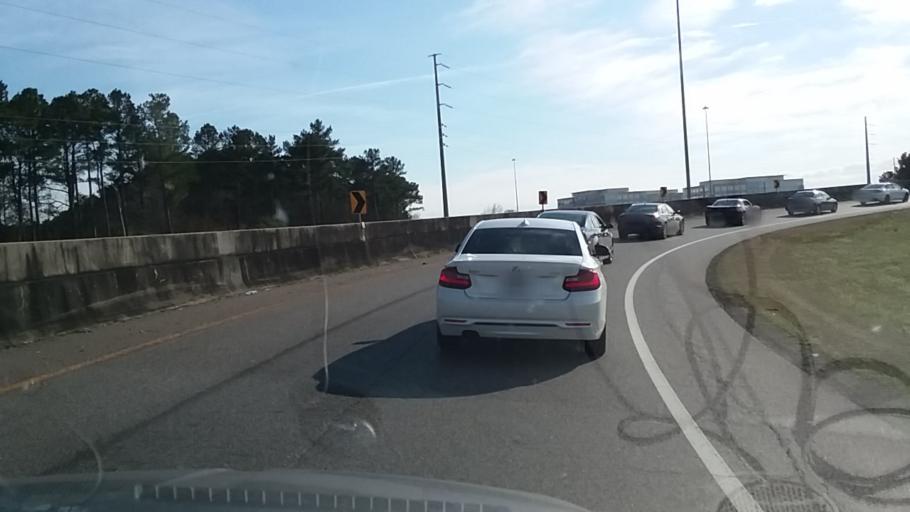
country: US
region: Alabama
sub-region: Madison County
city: Redstone Arsenal
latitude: 34.7057
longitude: -86.6695
